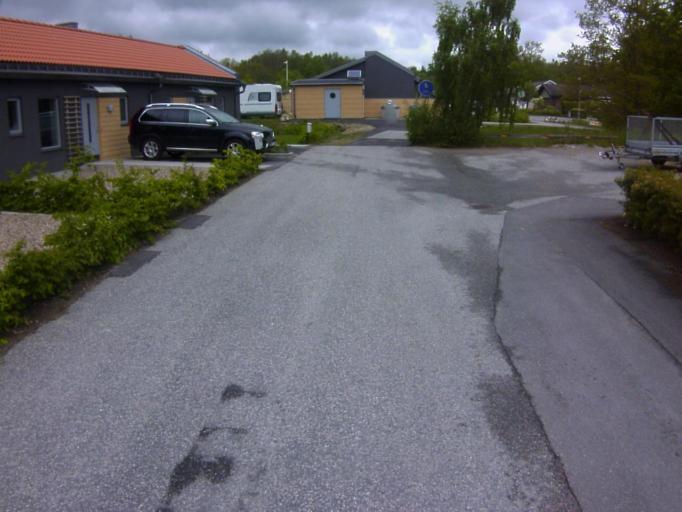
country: SE
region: Blekinge
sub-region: Solvesborgs Kommun
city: Soelvesborg
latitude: 56.0617
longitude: 14.5834
